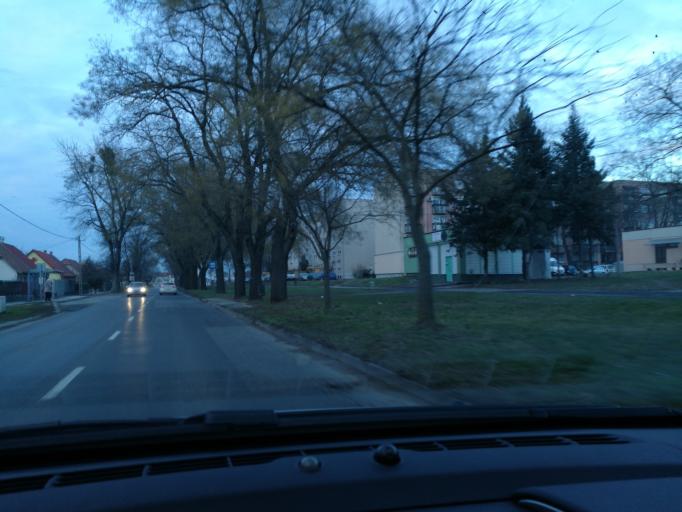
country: HU
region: Szabolcs-Szatmar-Bereg
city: Nyiregyhaza
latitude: 47.9591
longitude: 21.7356
